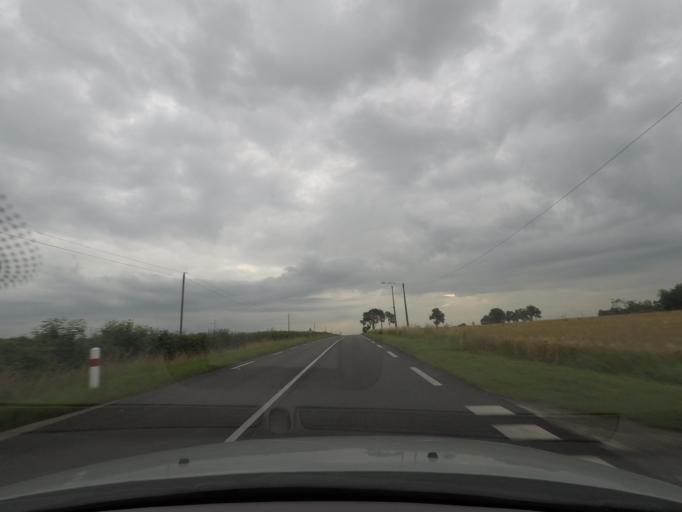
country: FR
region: Haute-Normandie
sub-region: Departement de la Seine-Maritime
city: Neufchatel-en-Bray
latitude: 49.7341
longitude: 1.5122
